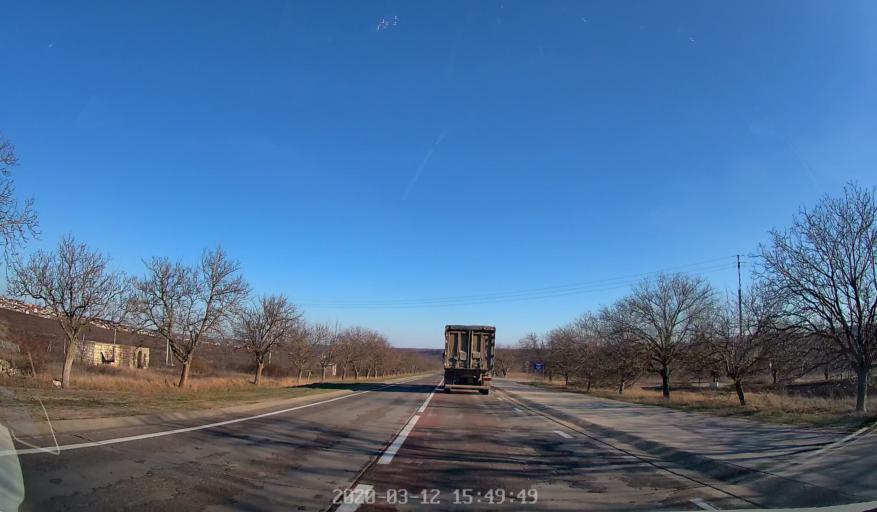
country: MD
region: Chisinau
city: Ciorescu
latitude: 47.0783
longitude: 28.9474
